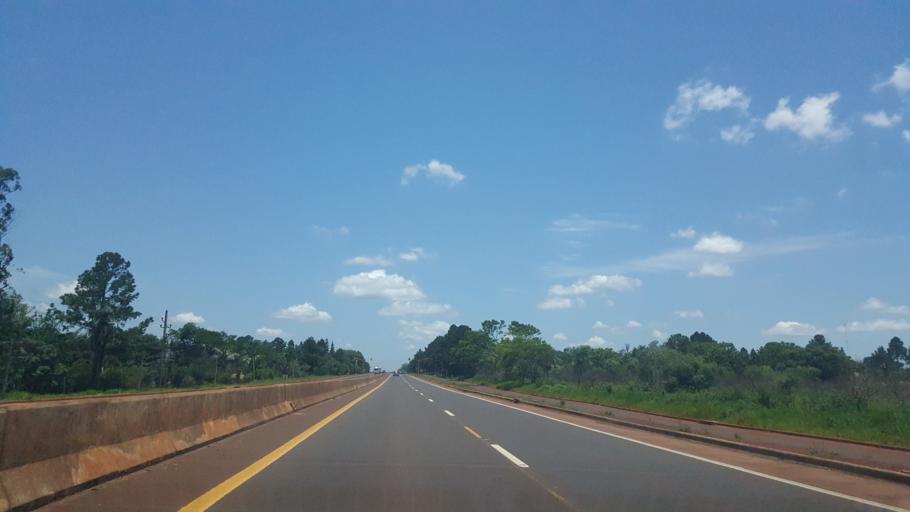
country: AR
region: Misiones
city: Garupa
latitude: -27.4925
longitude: -55.8643
